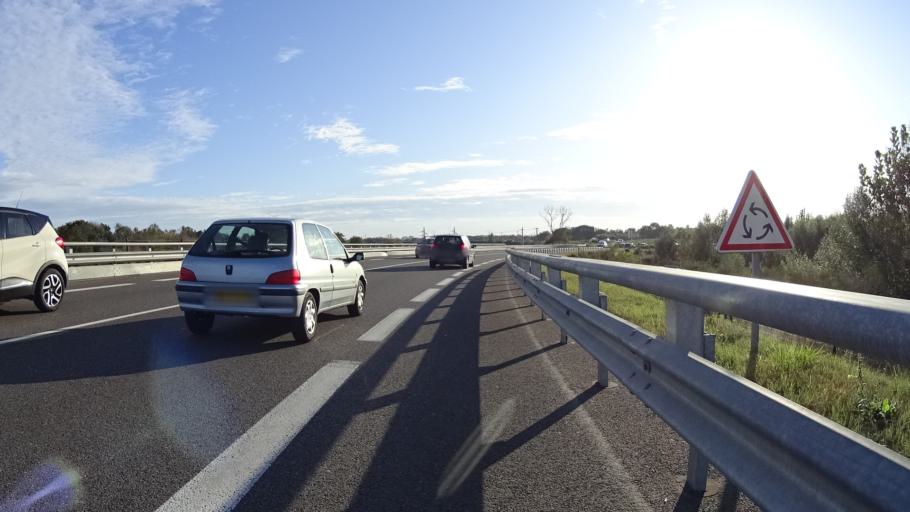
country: FR
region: Aquitaine
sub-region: Departement des Landes
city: Saint-Paul-les-Dax
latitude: 43.7253
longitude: -1.0359
